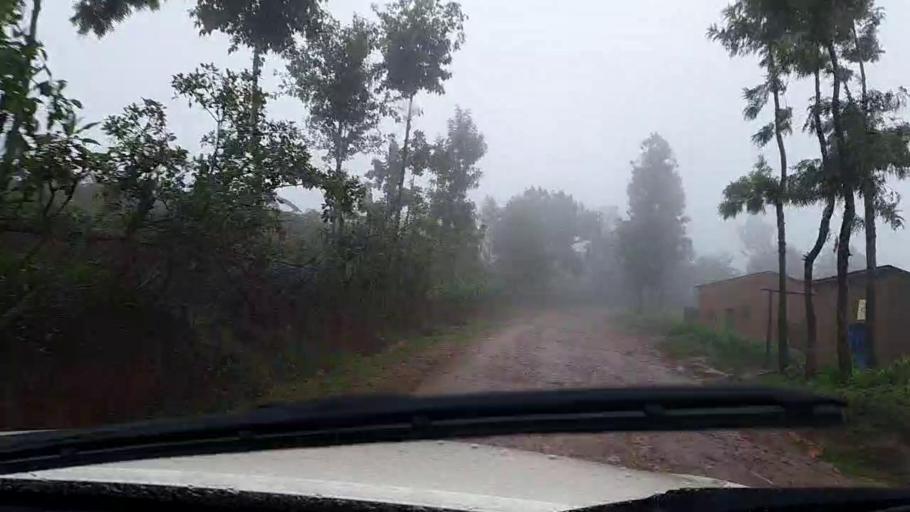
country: RW
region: Northern Province
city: Byumba
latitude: -1.7435
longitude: 30.0064
